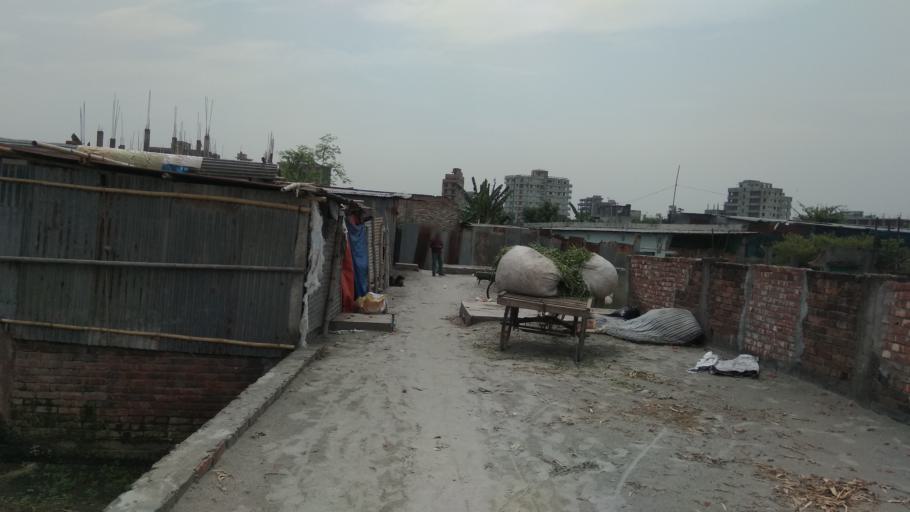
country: BD
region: Dhaka
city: Tungi
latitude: 23.8158
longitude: 90.3822
